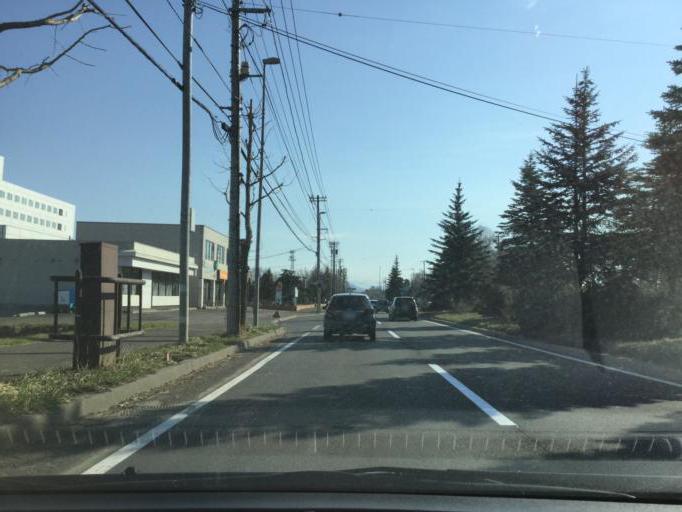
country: JP
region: Hokkaido
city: Iwamizawa
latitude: 43.1941
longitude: 141.7647
